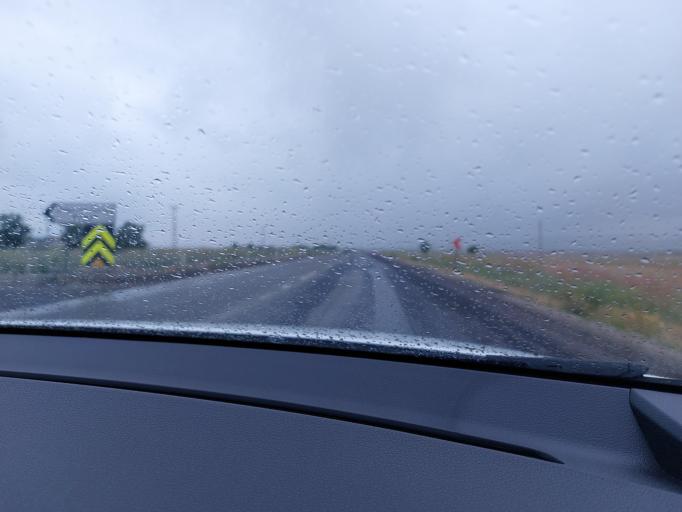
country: TR
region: Nevsehir
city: Dobada
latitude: 38.5325
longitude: 34.4402
